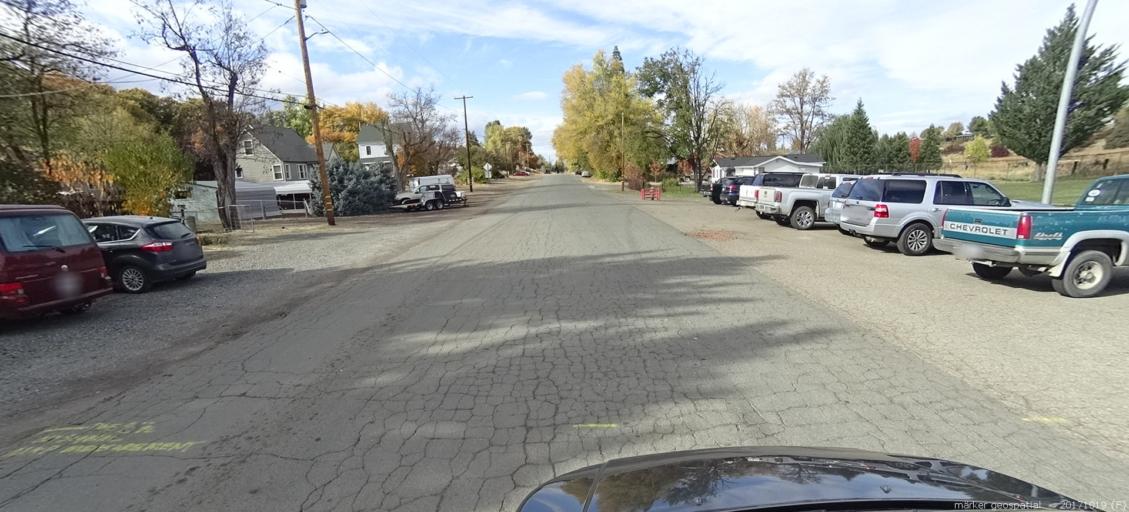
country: US
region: California
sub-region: Shasta County
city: Burney
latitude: 41.0032
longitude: -121.4434
